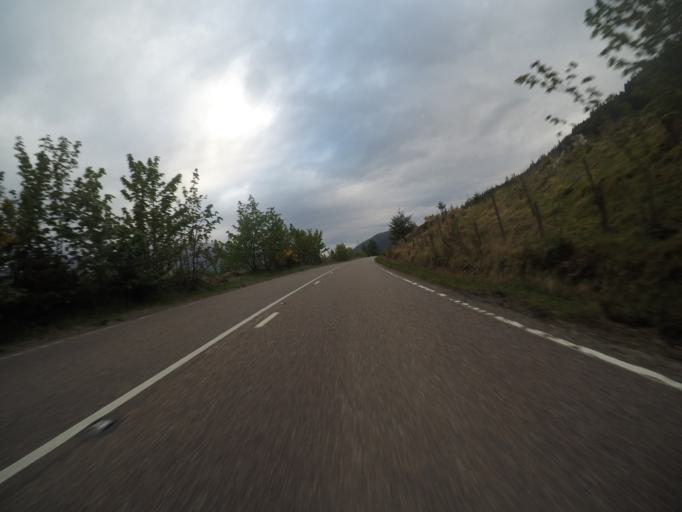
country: GB
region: Scotland
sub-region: Highland
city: Spean Bridge
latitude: 56.9249
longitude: -4.9401
